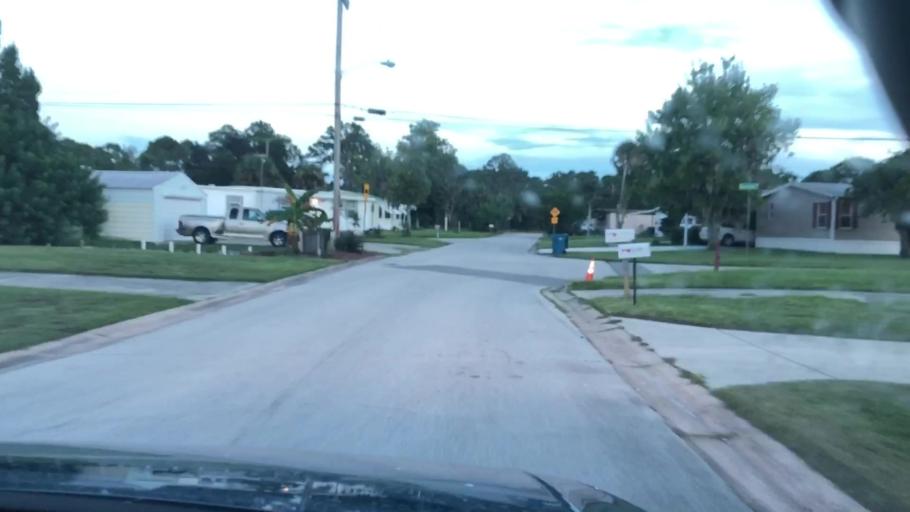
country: US
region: Florida
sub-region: Volusia County
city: Oak Hill
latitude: 28.9127
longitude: -80.8664
